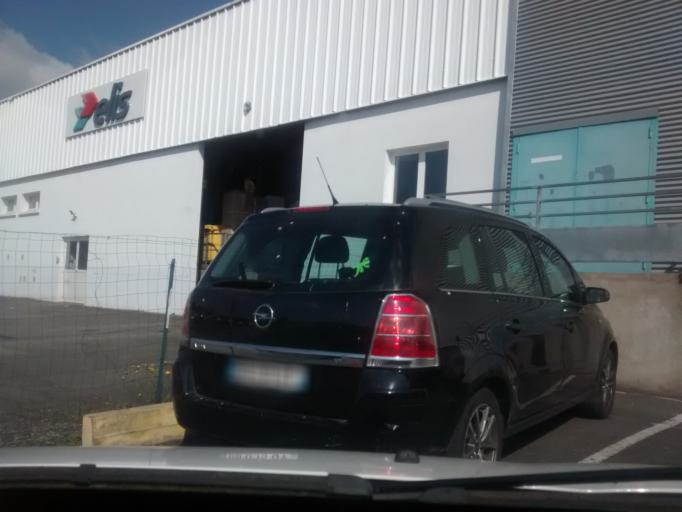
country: FR
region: Brittany
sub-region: Departement d'Ille-et-Vilaine
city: Saint-Gregoire
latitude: 48.1385
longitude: -1.6914
